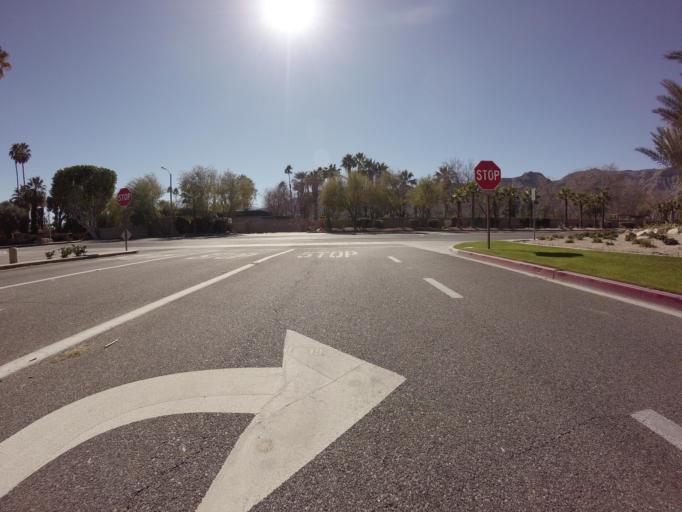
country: US
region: California
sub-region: Riverside County
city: Rancho Mirage
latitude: 33.7582
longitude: -116.4257
